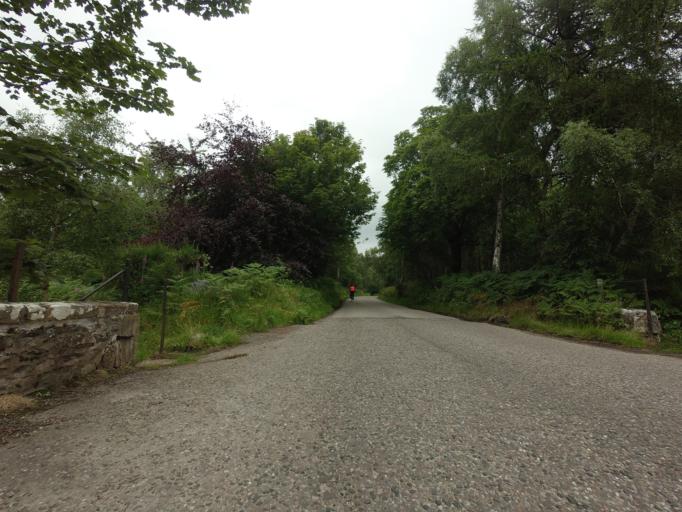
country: GB
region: Scotland
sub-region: Highland
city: Evanton
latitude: 57.8862
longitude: -4.3878
